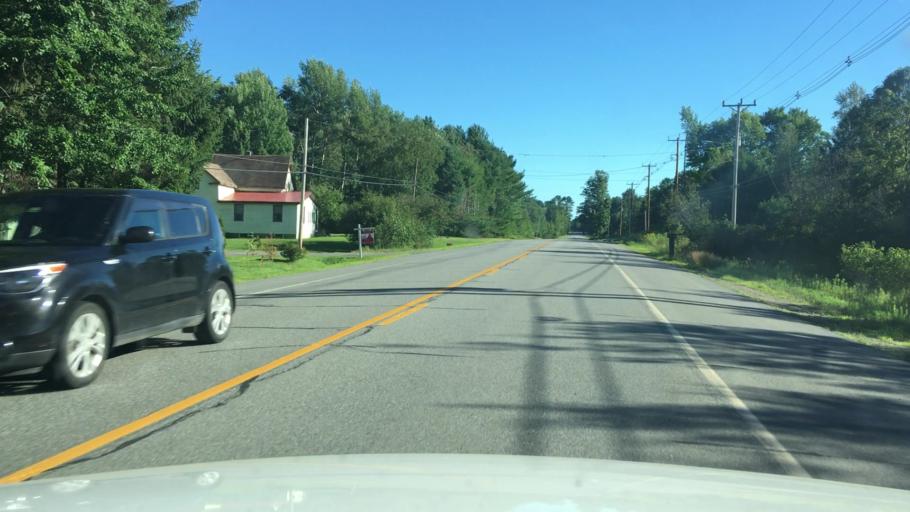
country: US
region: Maine
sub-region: Penobscot County
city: Howland
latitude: 45.1809
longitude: -68.6180
